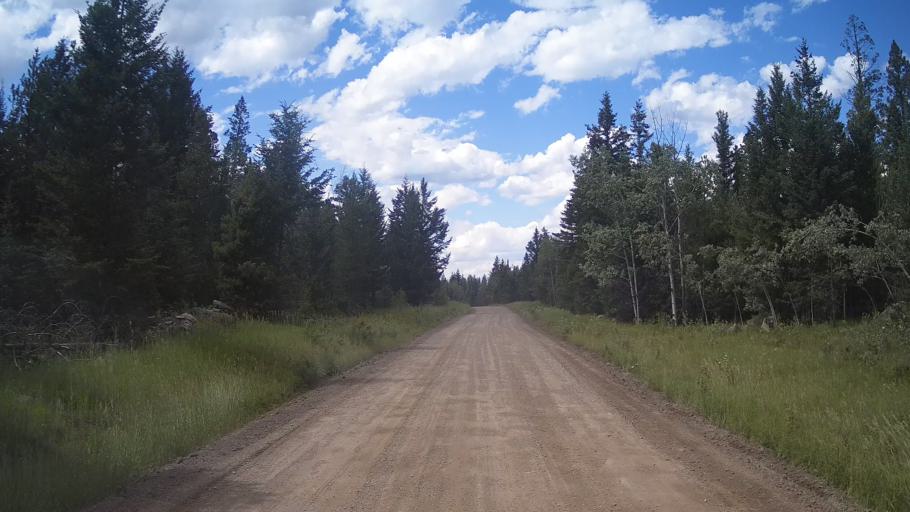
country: CA
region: British Columbia
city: Lillooet
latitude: 51.3223
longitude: -121.8669
